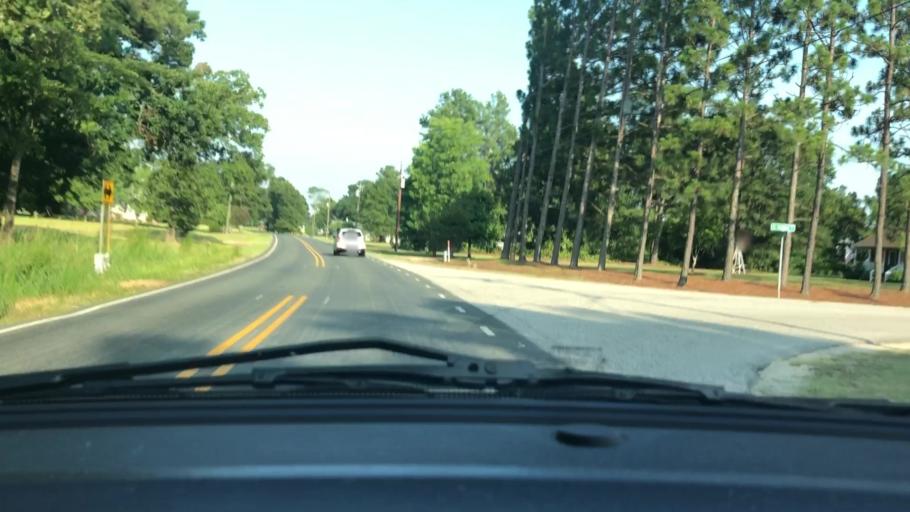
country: US
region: North Carolina
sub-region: Lee County
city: Broadway
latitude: 35.3480
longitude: -79.0694
